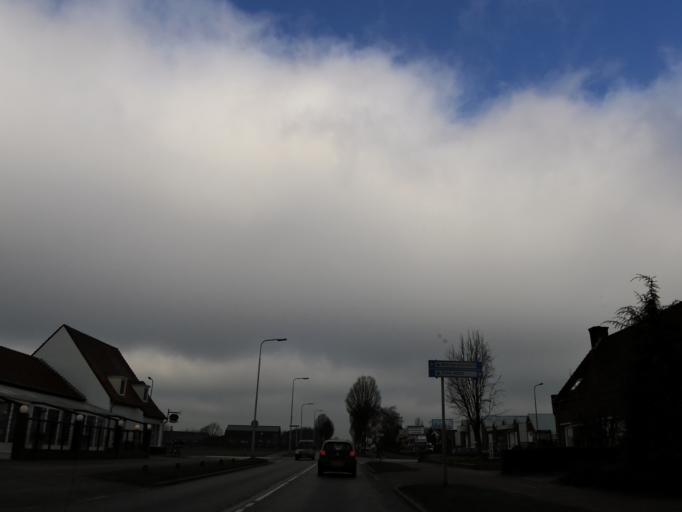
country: NL
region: Limburg
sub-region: Gemeente Venray
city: Venray
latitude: 51.4910
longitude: 5.8955
